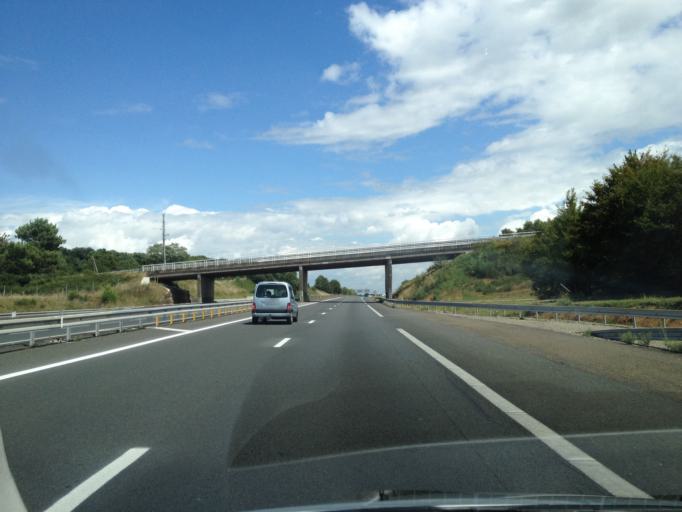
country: FR
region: Pays de la Loire
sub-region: Departement de la Sarthe
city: La Chapelle-Saint-Aubin
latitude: 48.0417
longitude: 0.1494
